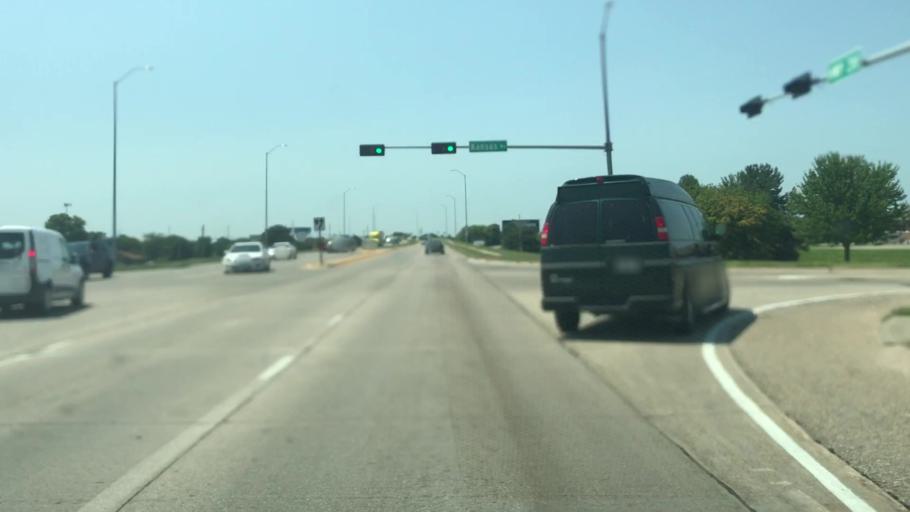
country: US
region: Nebraska
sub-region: Adams County
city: Hastings
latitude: 40.6090
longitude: -98.3863
